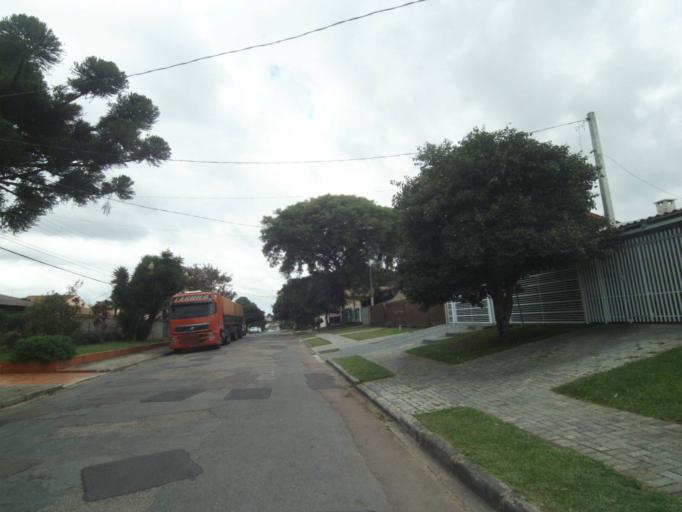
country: BR
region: Parana
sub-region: Pinhais
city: Pinhais
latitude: -25.4432
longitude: -49.2188
